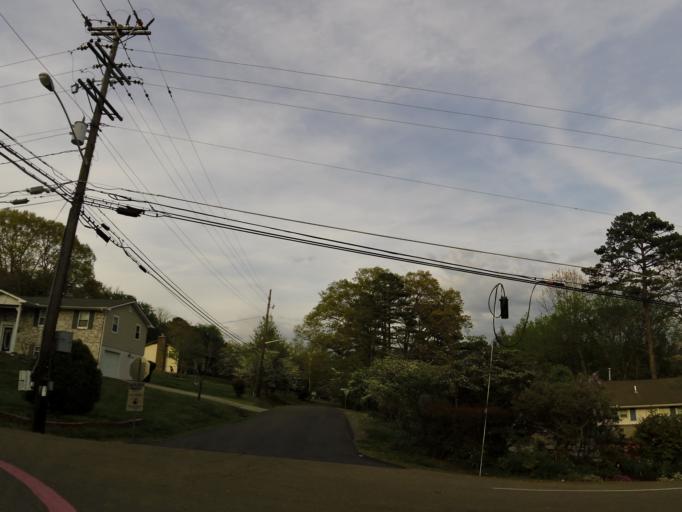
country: US
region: Tennessee
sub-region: Knox County
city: Knoxville
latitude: 36.0508
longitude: -83.9114
